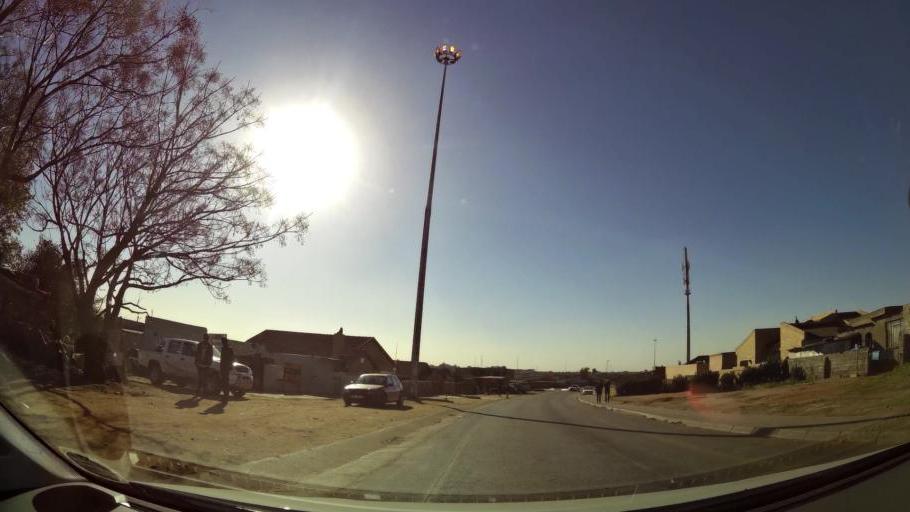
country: ZA
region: Gauteng
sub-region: Ekurhuleni Metropolitan Municipality
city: Tembisa
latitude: -26.0184
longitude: 28.2247
